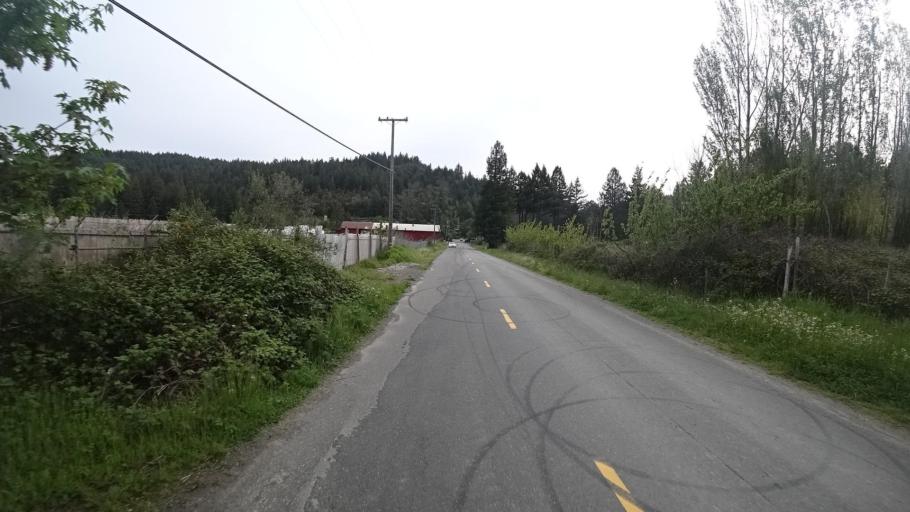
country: US
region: California
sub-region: Humboldt County
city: Redway
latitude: 40.2648
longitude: -123.8748
